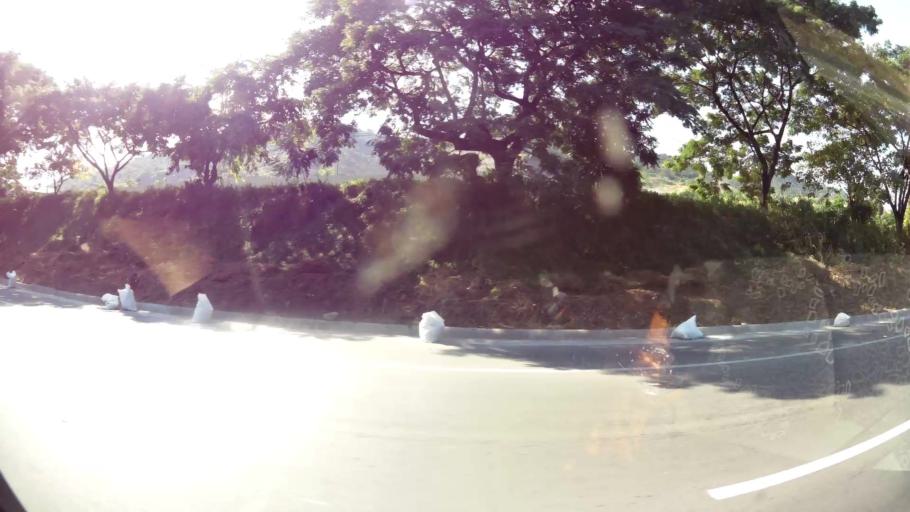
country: EC
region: Guayas
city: Santa Lucia
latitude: -2.1839
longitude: -80.0014
